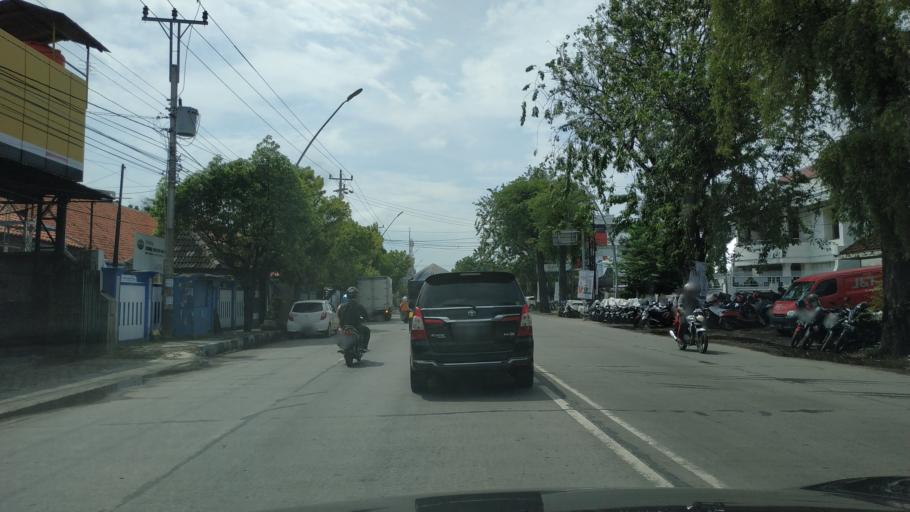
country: ID
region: Central Java
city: Tegal
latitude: -6.8654
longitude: 109.1338
